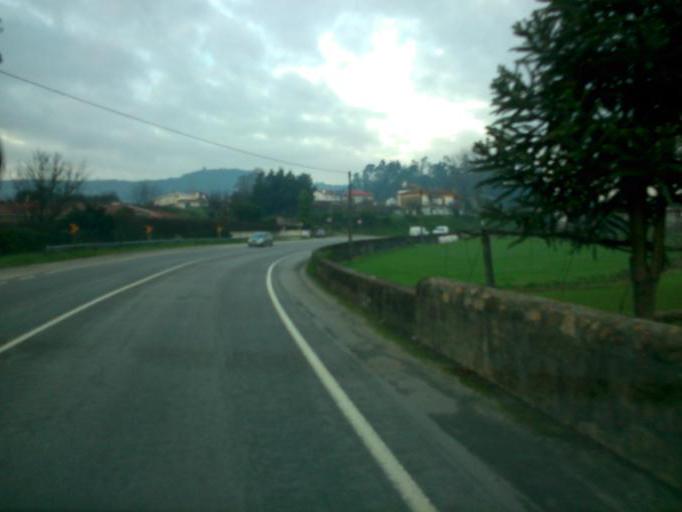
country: PT
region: Braga
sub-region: Barcelos
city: Barcelos
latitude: 41.5074
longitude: -8.5799
